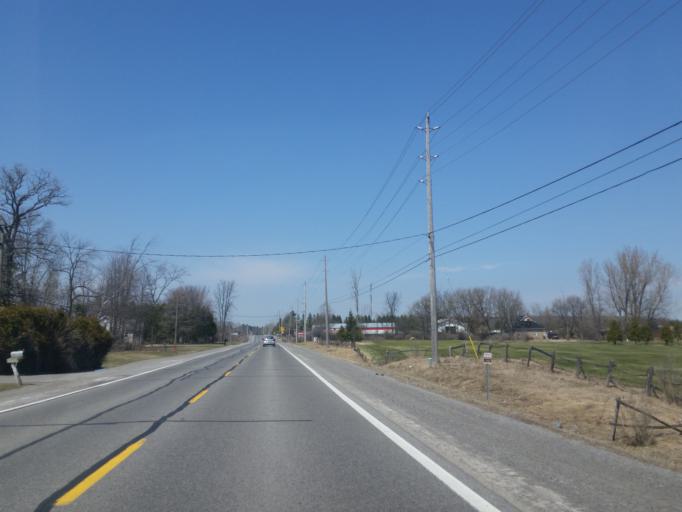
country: CA
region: Ontario
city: Bells Corners
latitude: 45.4570
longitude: -76.0682
